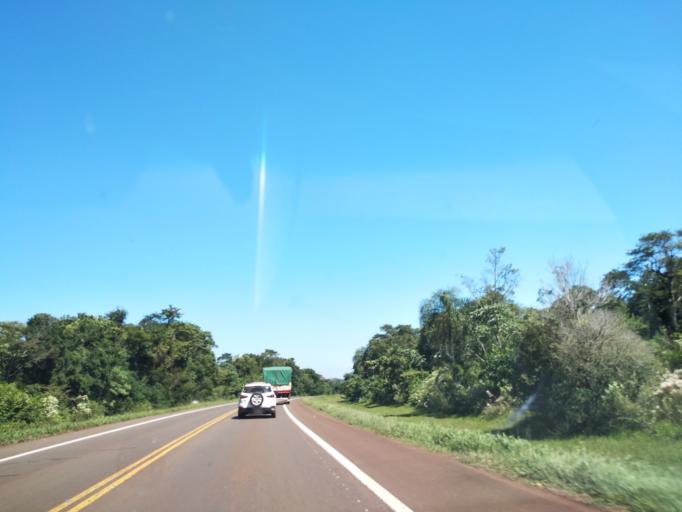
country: AR
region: Misiones
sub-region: Departamento de Iguazu
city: Puerto Iguazu
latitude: -25.7400
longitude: -54.5351
